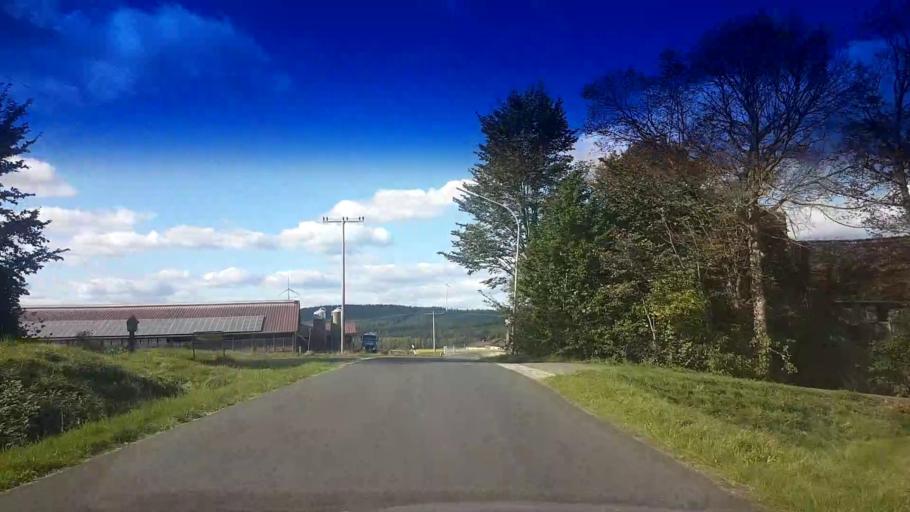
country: DE
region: Bavaria
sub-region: Upper Franconia
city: Schirnding
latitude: 50.0241
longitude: 12.2352
